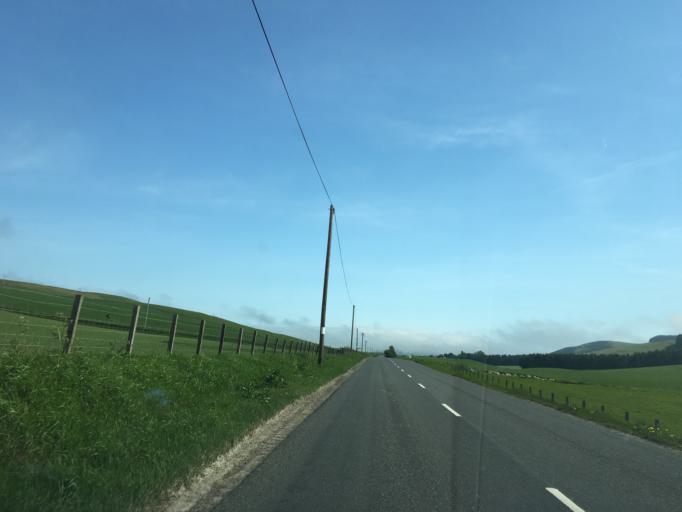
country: GB
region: Scotland
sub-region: South Lanarkshire
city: Biggar
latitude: 55.6660
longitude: -3.4240
